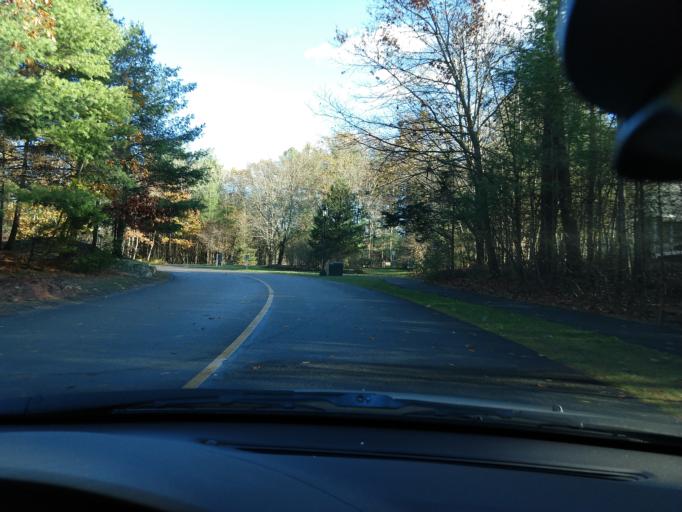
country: US
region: Massachusetts
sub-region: Middlesex County
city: Bedford
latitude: 42.4985
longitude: -71.2593
